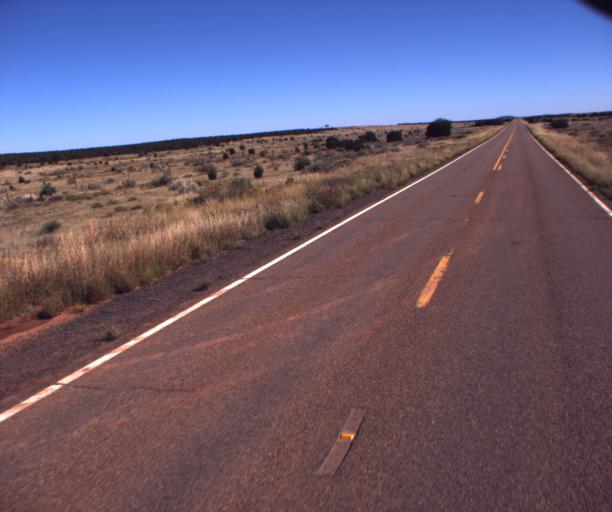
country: US
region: Arizona
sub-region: Navajo County
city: Heber-Overgaard
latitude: 34.4729
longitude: -110.3571
